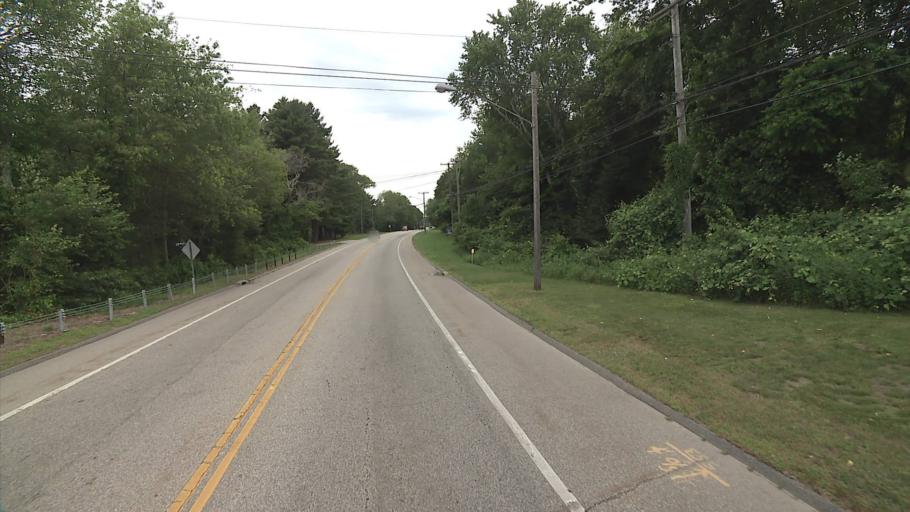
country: US
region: Connecticut
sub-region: New London County
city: Poquonock Bridge
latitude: 41.3534
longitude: -72.0296
